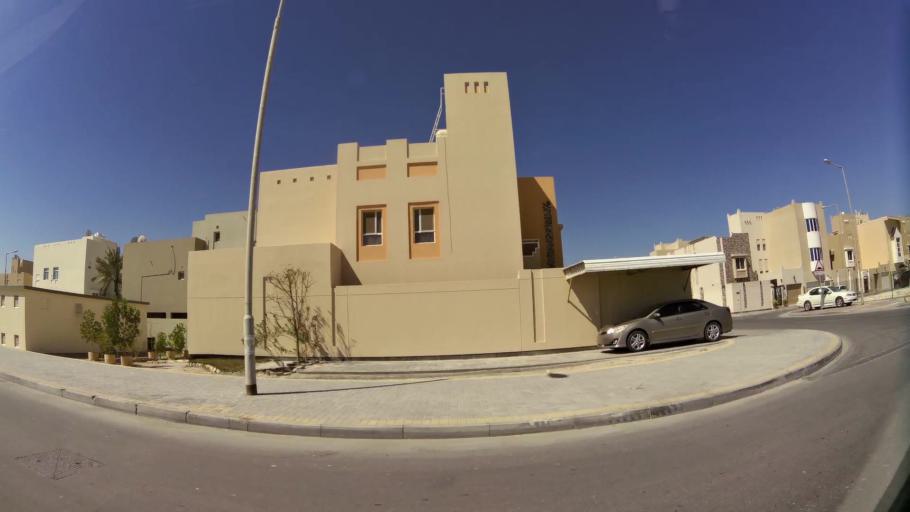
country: BH
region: Muharraq
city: Al Muharraq
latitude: 26.2747
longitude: 50.5986
